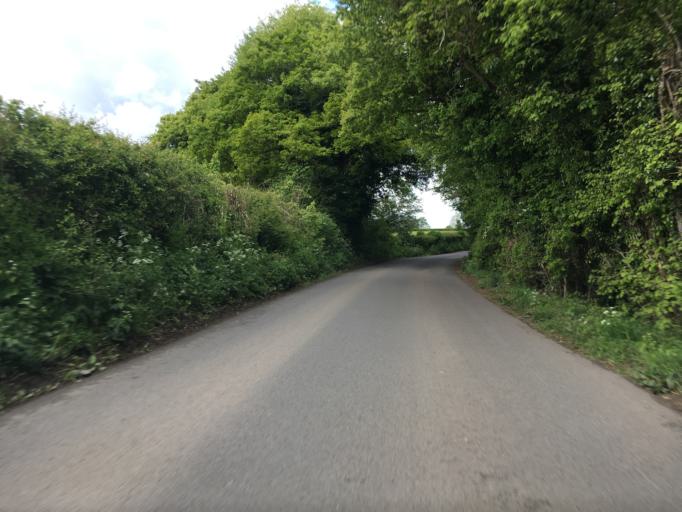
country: GB
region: England
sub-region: Gloucestershire
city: Stonehouse
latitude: 51.7743
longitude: -2.2953
